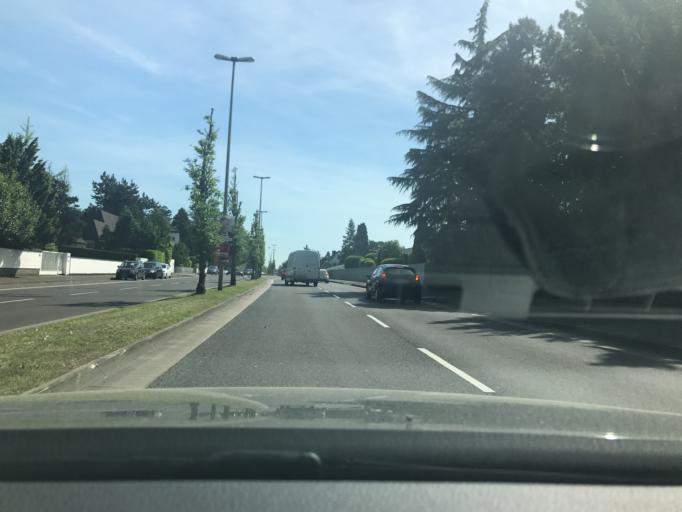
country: DE
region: North Rhine-Westphalia
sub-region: Regierungsbezirk Dusseldorf
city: Monchengladbach
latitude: 51.2105
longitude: 6.4343
